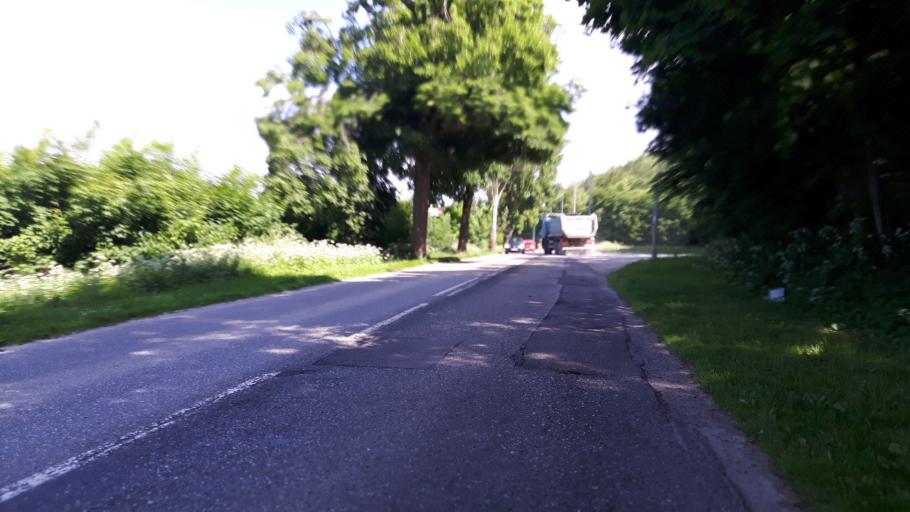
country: PL
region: Pomeranian Voivodeship
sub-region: Powiat wejherowski
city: Orle
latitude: 54.6471
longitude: 18.1115
